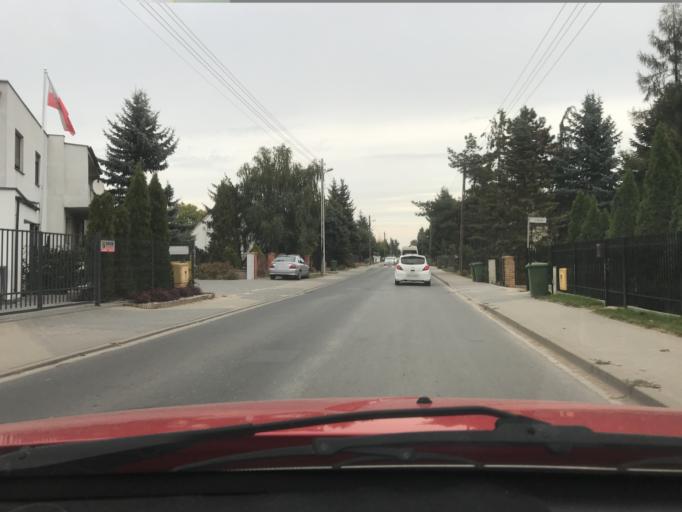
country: PL
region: Greater Poland Voivodeship
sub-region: Powiat poznanski
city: Plewiska
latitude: 52.3644
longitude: 16.8176
